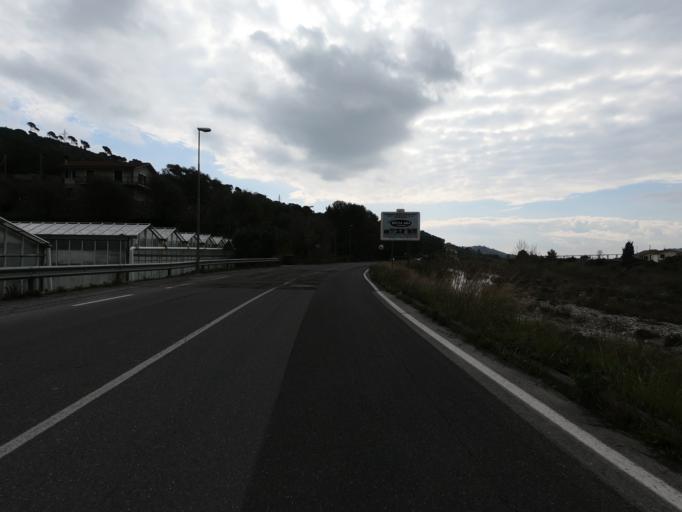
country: IT
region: Liguria
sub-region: Provincia di Savona
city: Laigueglia
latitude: 43.9839
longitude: 8.1321
